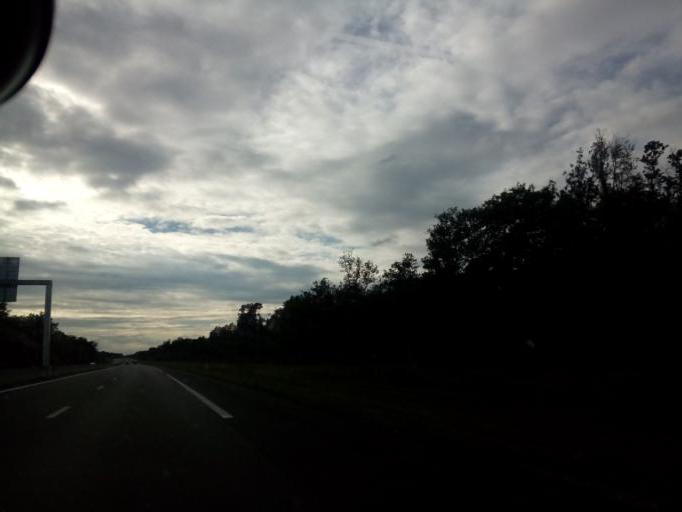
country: FR
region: Centre
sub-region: Departement d'Indre-et-Loire
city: Esvres
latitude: 47.3094
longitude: 0.7970
